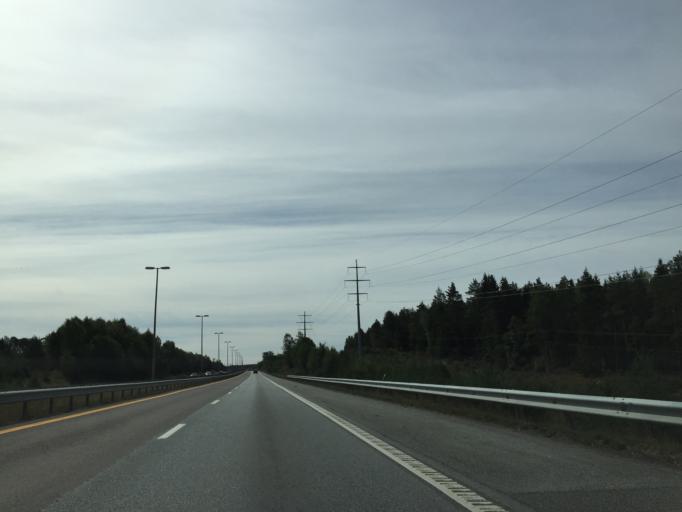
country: NO
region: Akershus
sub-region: Vestby
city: Vestby
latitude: 59.5555
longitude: 10.7216
